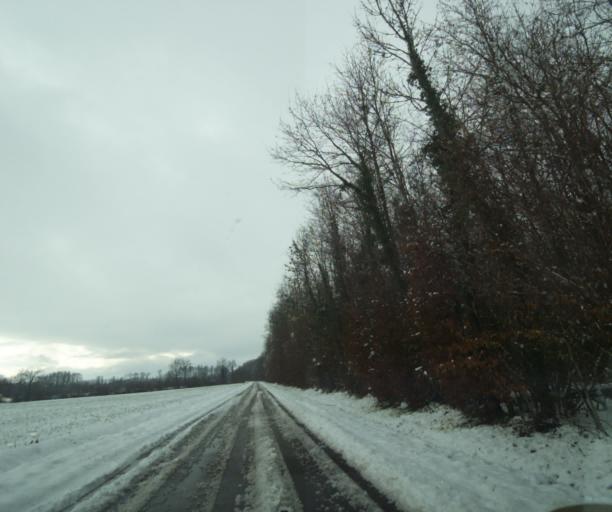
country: FR
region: Champagne-Ardenne
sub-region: Departement de la Haute-Marne
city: Montier-en-Der
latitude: 48.4787
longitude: 4.6652
